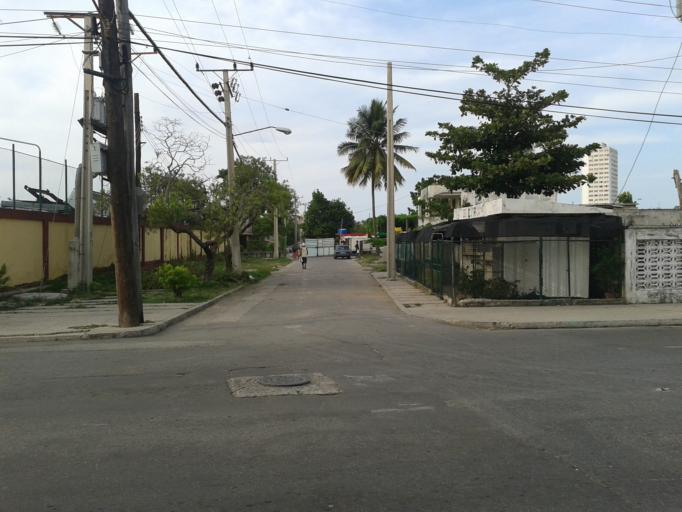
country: CU
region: La Habana
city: Cerro
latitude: 23.1204
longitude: -82.3779
